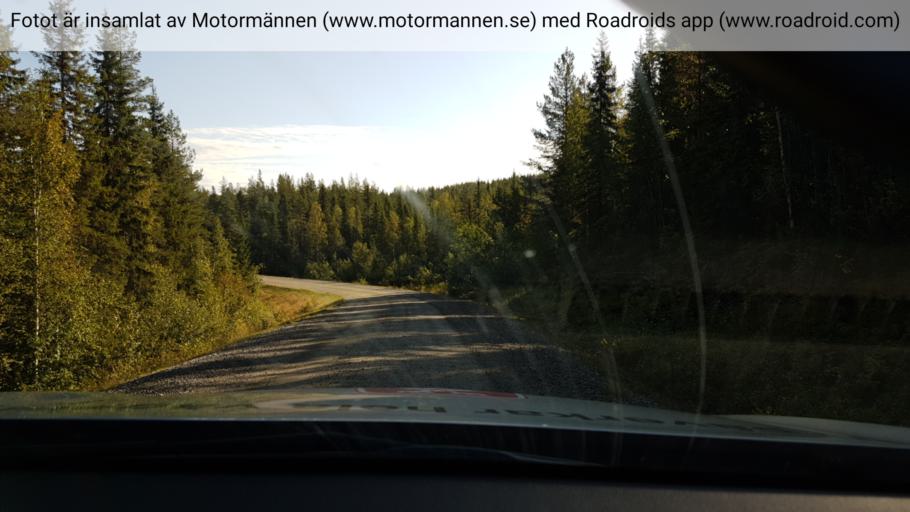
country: SE
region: Vaesterbotten
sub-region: Norsjo Kommun
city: Norsjoe
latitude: 64.7103
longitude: 19.5320
